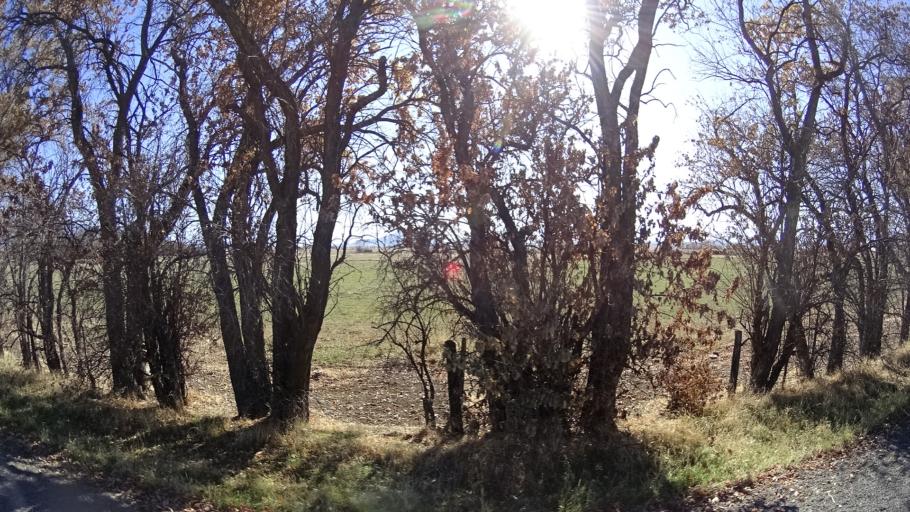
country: US
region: California
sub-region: Siskiyou County
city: Montague
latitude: 41.7263
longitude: -122.3935
